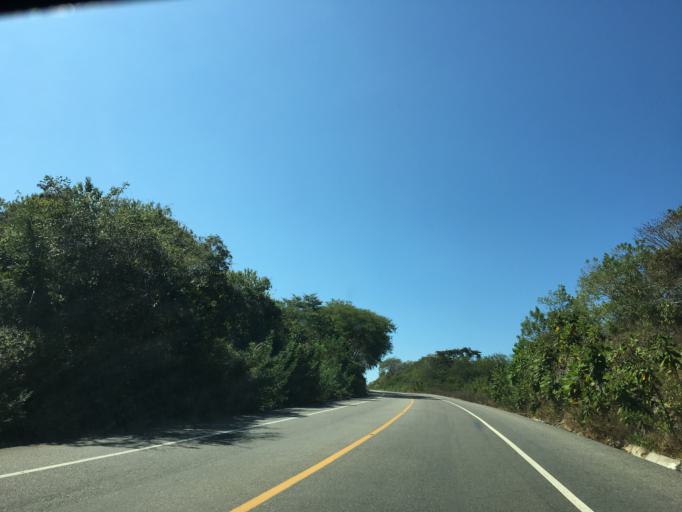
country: MX
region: Oaxaca
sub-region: Santa Maria Huatulco
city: Sector H Tres
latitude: 15.7741
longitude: -96.2387
